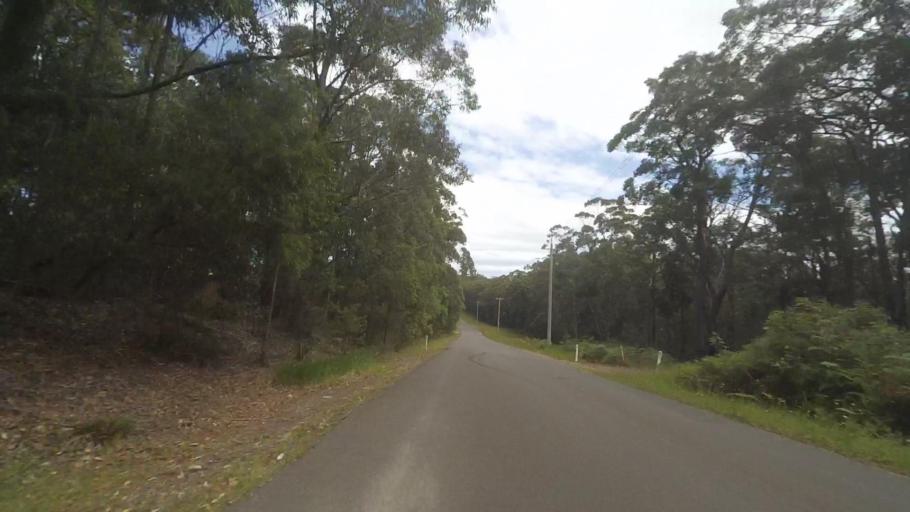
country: AU
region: New South Wales
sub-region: Shoalhaven Shire
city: Milton
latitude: -35.3783
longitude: 150.3744
